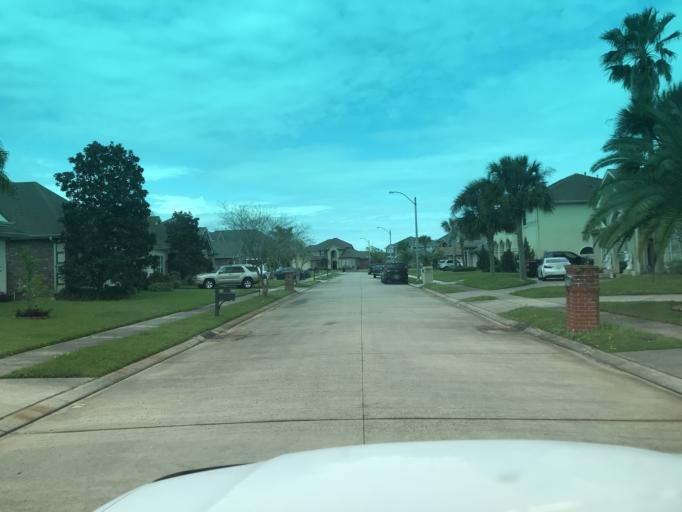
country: US
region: Louisiana
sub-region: Saint Bernard Parish
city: Chalmette
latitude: 30.0339
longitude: -89.9492
